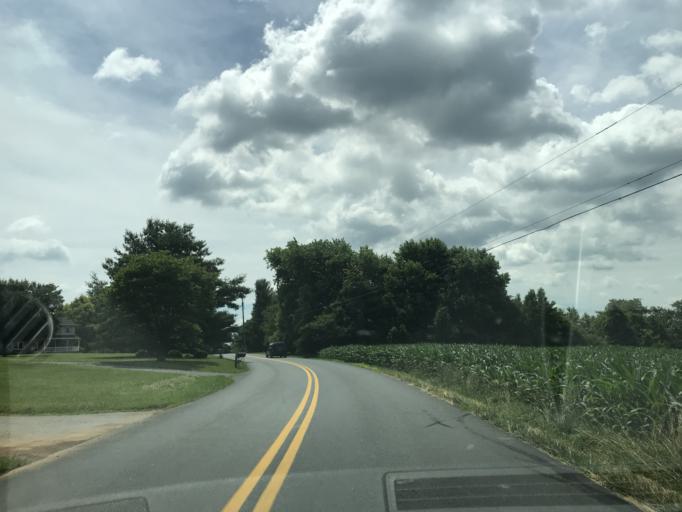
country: US
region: Maryland
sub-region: Carroll County
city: Hampstead
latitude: 39.6353
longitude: -76.8059
